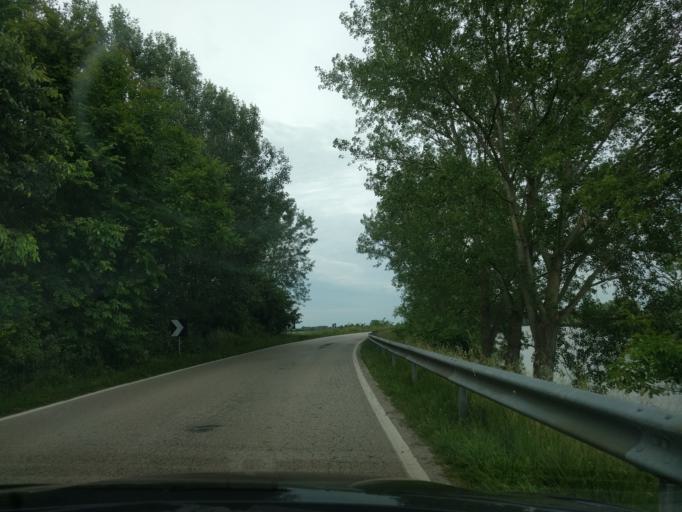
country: IT
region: Veneto
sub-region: Provincia di Rovigo
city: Gavello
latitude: 45.0370
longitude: 11.9568
